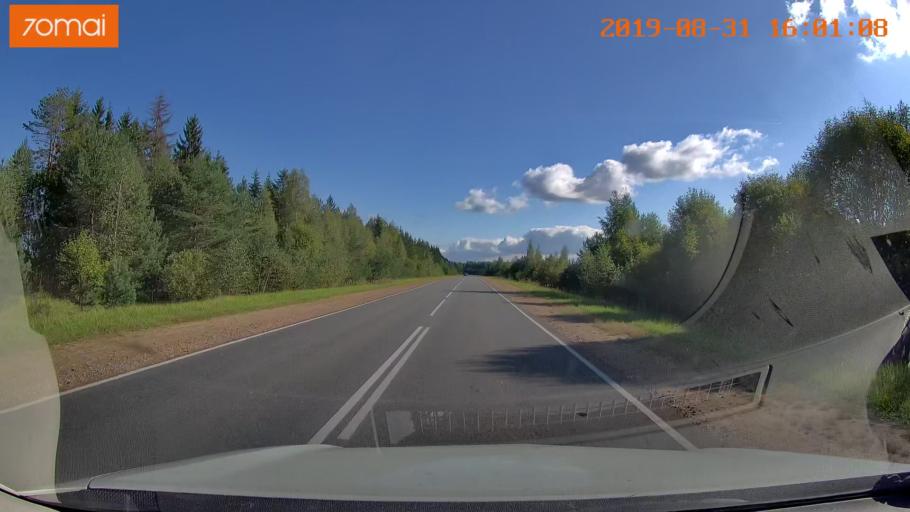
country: RU
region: Kaluga
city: Yukhnov
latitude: 54.6943
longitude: 35.2884
